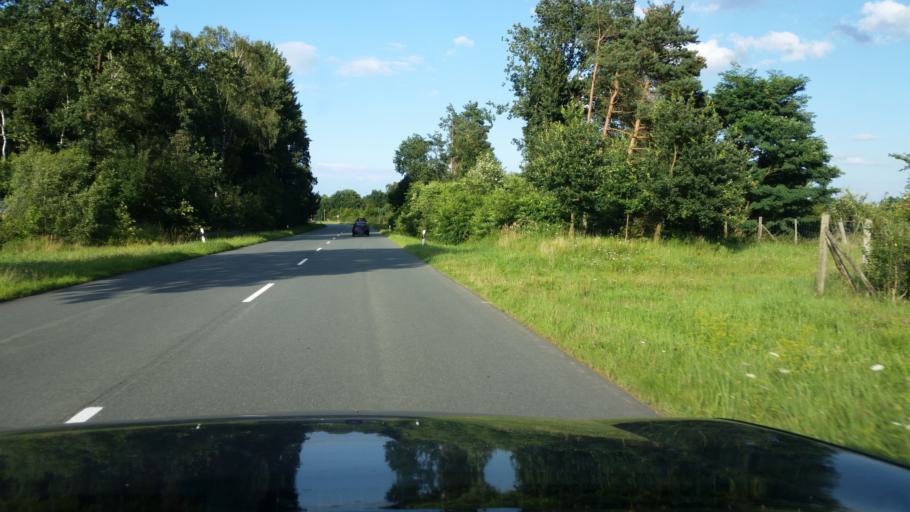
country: DE
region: Lower Saxony
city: Bad Fallingbostel
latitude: 52.8397
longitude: 9.7116
